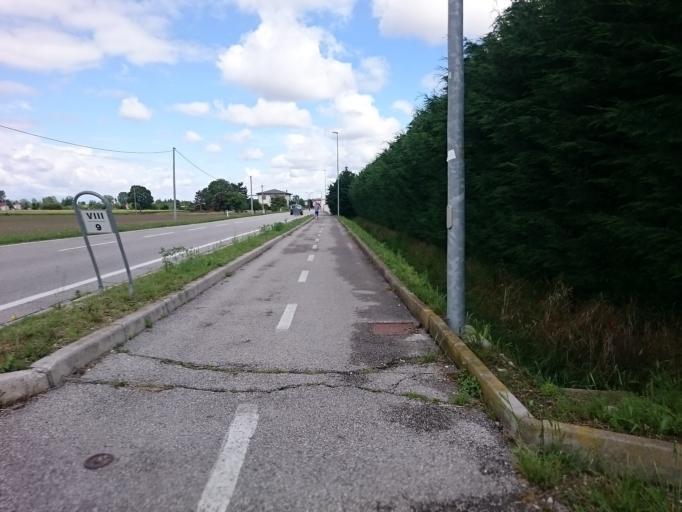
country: IT
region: Veneto
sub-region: Provincia di Padova
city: Mestrino
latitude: 45.4529
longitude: 11.7530
